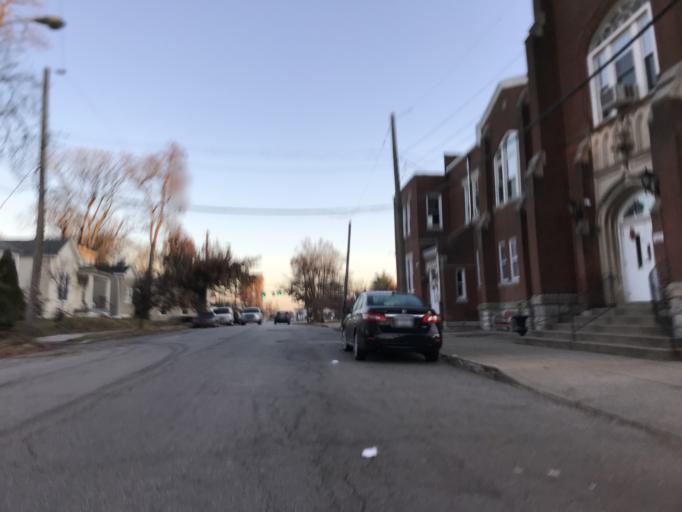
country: US
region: Kentucky
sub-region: Jefferson County
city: Louisville
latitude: 38.2339
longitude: -85.7433
